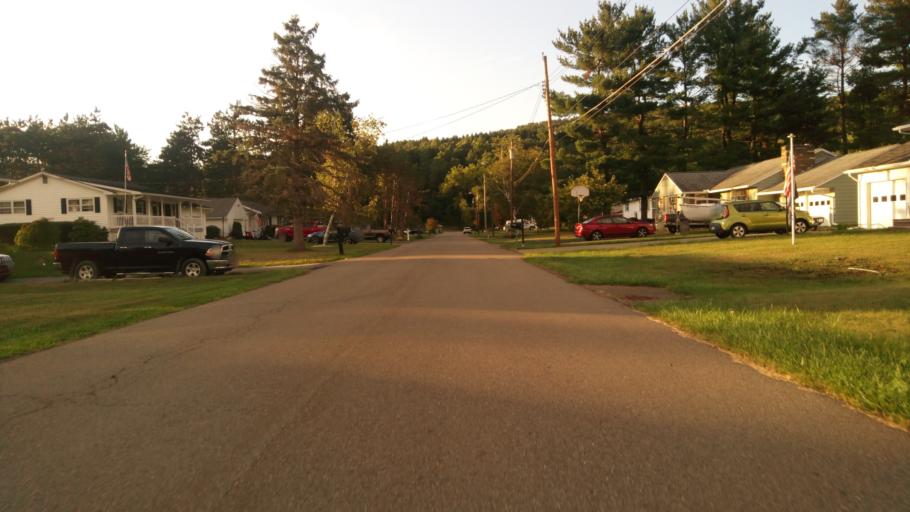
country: US
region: New York
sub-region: Chemung County
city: Southport
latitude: 42.0560
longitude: -76.8287
